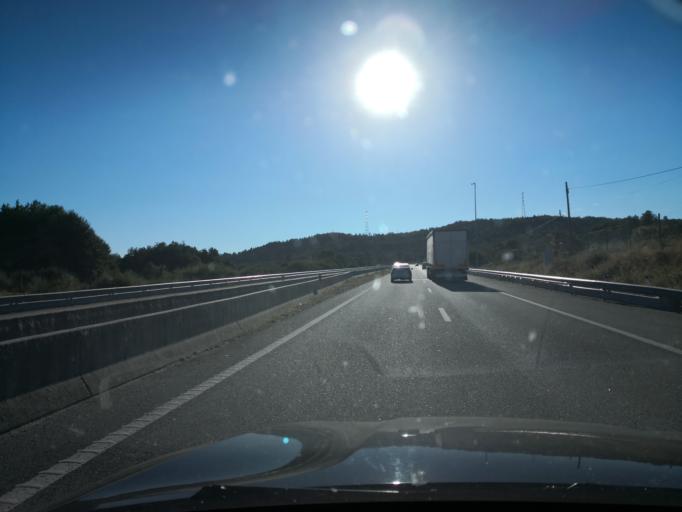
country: PT
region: Vila Real
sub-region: Sabrosa
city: Sabrosa
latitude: 41.3423
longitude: -7.6124
